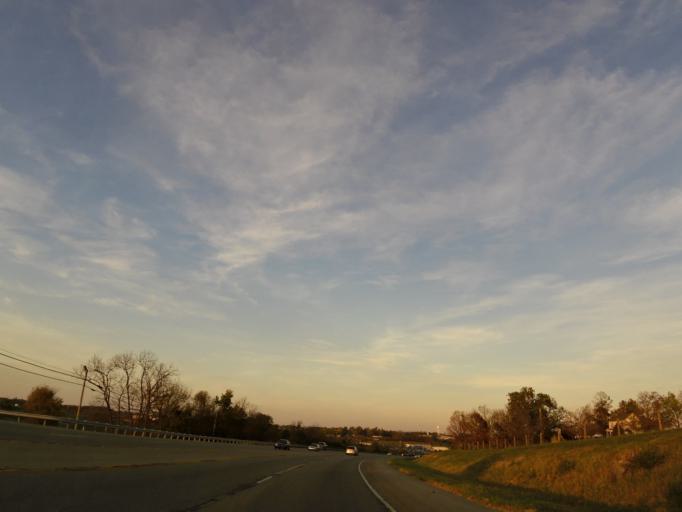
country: US
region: Kentucky
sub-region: Jessamine County
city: Nicholasville
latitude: 37.9246
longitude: -84.5526
